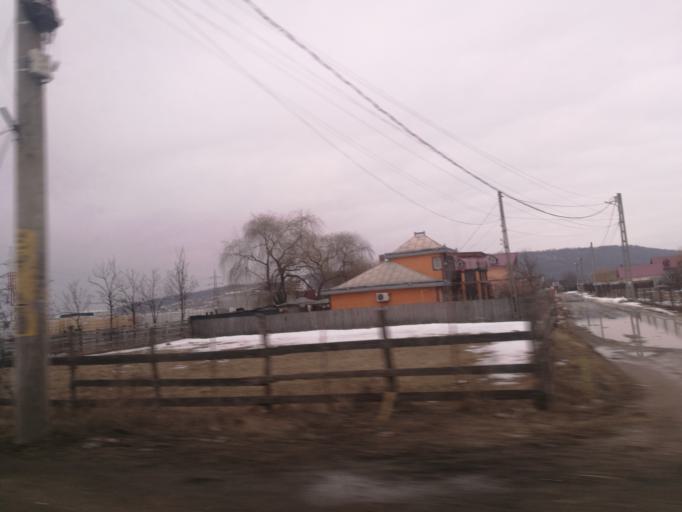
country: RO
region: Iasi
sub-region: Comuna Podu Iloaiei
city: Podu Iloaiei
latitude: 47.2147
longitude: 27.2863
